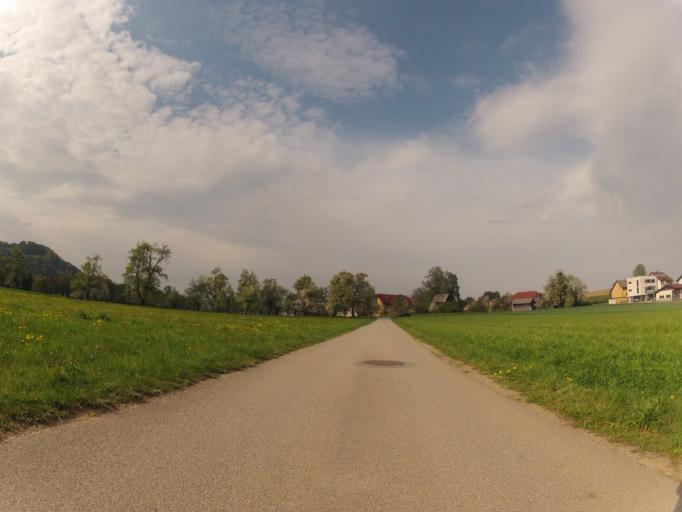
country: AT
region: Upper Austria
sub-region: Politischer Bezirk Gmunden
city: Altmunster
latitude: 47.9332
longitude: 13.7591
